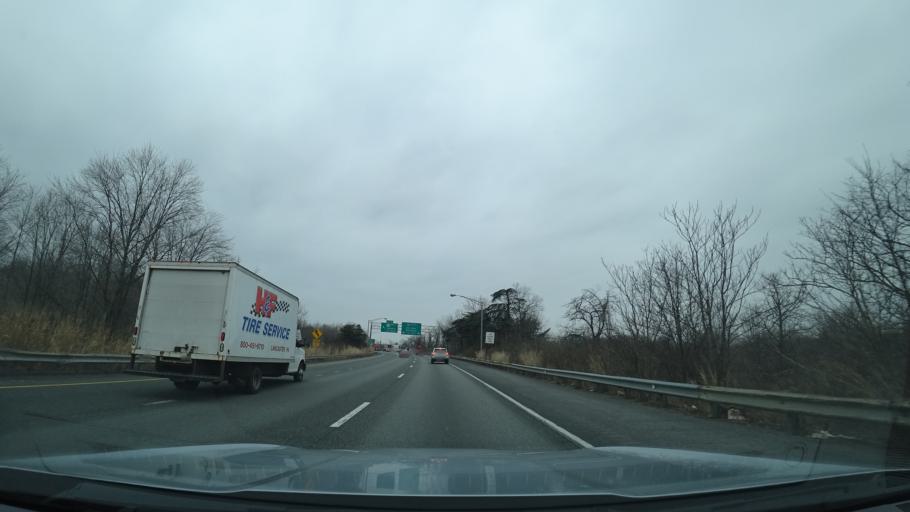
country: US
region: Delaware
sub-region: New Castle County
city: Newport
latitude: 39.7072
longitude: -75.5954
